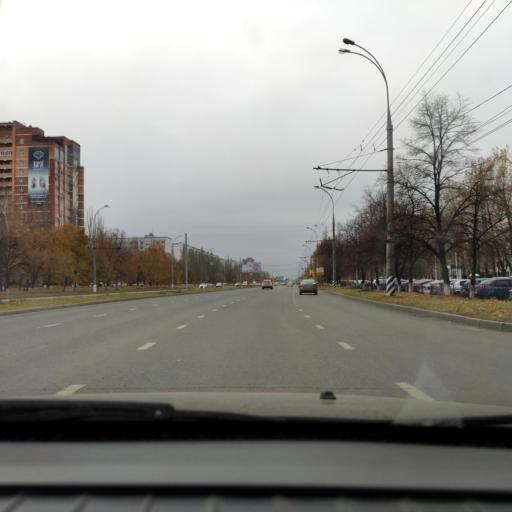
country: RU
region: Samara
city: Tol'yatti
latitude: 53.5156
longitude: 49.2938
